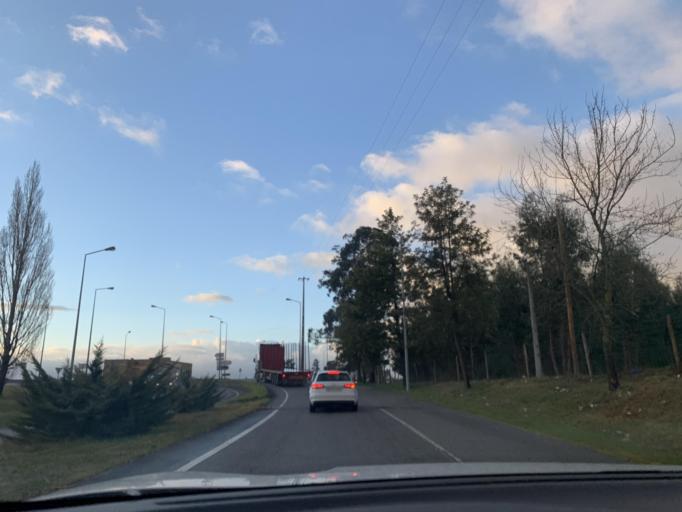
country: PT
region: Viseu
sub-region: Concelho de Tondela
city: Tondela
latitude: 40.4998
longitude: -8.0834
